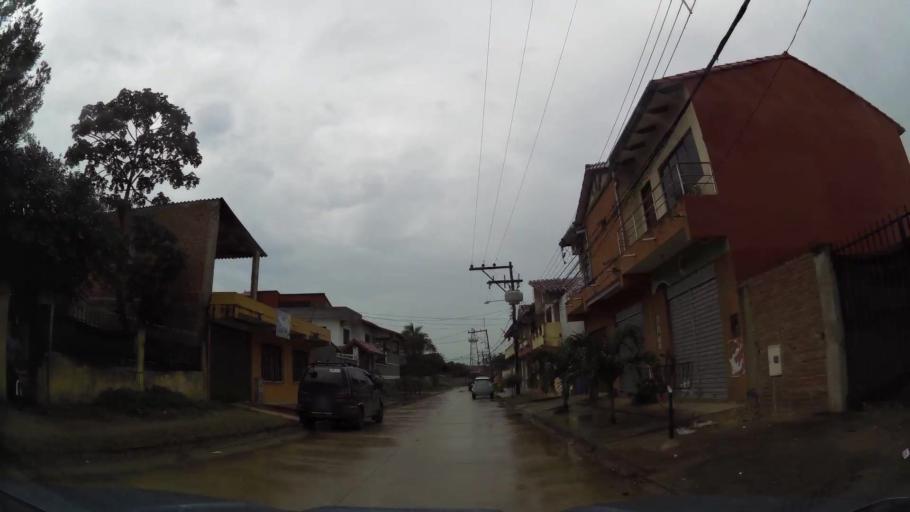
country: BO
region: Santa Cruz
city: Santa Cruz de la Sierra
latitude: -17.8154
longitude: -63.2256
